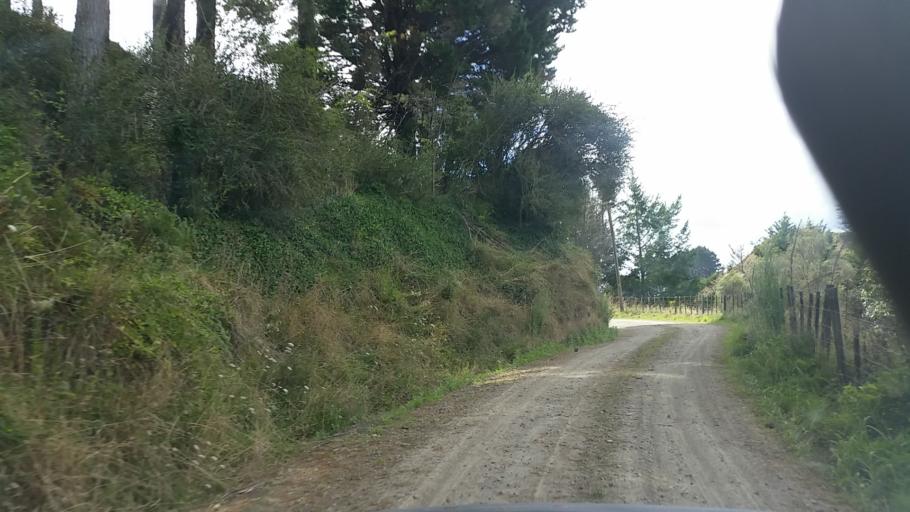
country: NZ
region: Taranaki
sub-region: South Taranaki District
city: Eltham
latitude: -39.2528
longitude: 174.5666
